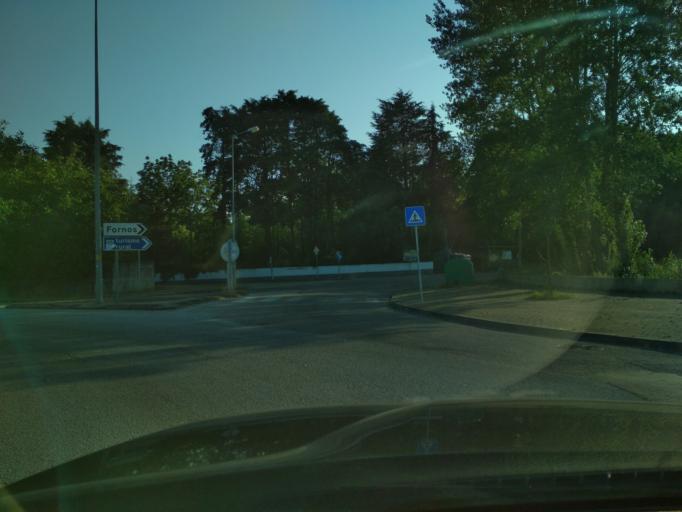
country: PT
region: Coimbra
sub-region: Coimbra
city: Coimbra
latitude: 40.2675
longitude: -8.4445
